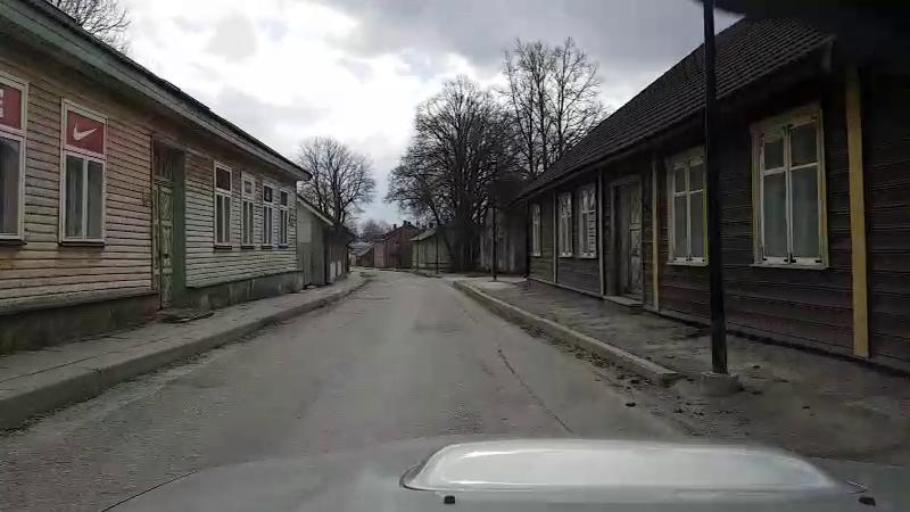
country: EE
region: Jaervamaa
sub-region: Paide linn
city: Paide
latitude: 58.8851
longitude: 25.5706
